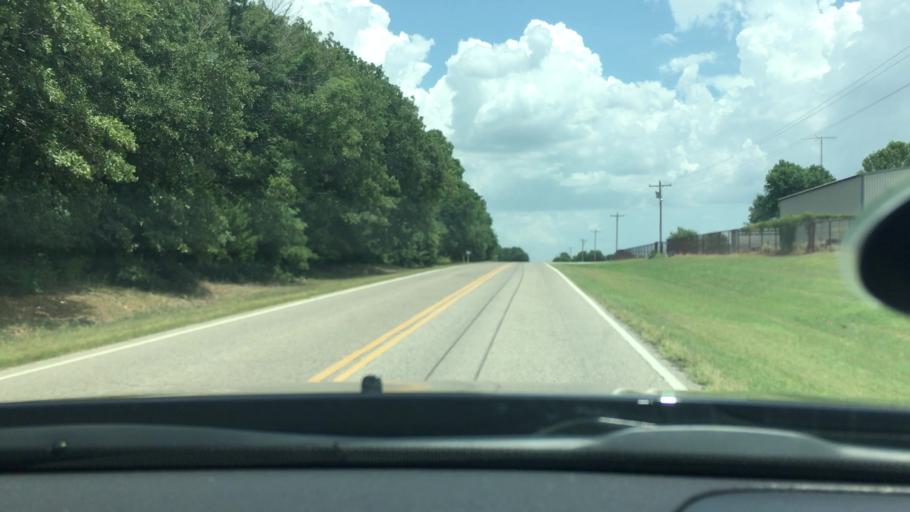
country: US
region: Oklahoma
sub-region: Love County
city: Marietta
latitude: 33.9839
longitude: -96.9681
